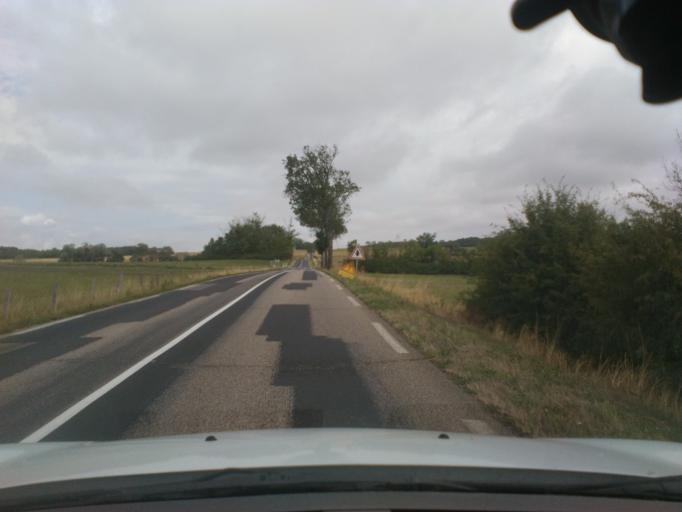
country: FR
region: Lorraine
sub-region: Departement de Meurthe-et-Moselle
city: Vezelise
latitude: 48.4312
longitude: 6.1246
